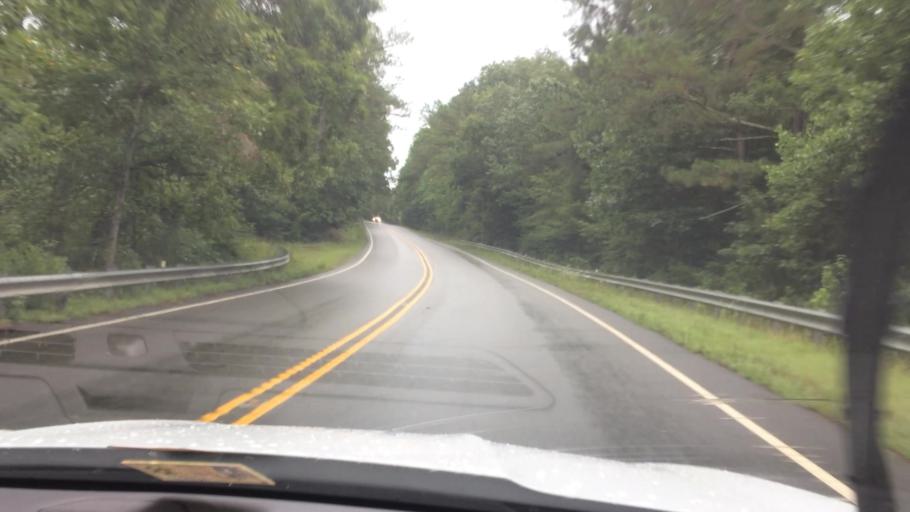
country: US
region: Virginia
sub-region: King William County
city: West Point
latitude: 37.5579
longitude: -76.7440
